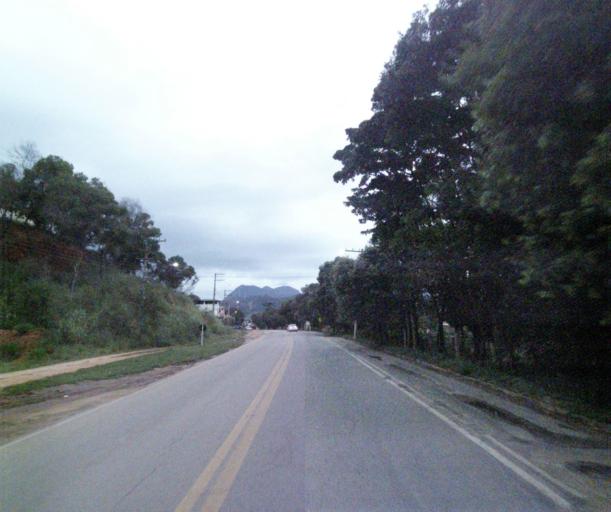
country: BR
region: Espirito Santo
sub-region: Castelo
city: Castelo
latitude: -20.6339
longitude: -41.2062
